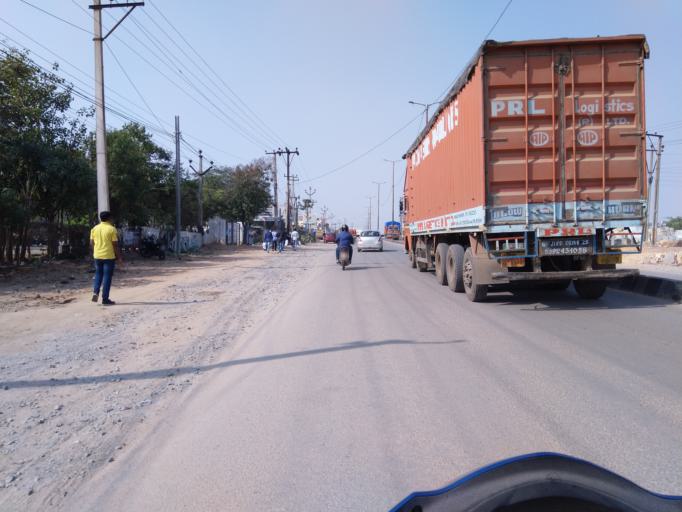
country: IN
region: Telangana
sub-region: Rangareddi
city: Quthbullapur
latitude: 17.5347
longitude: 78.4352
